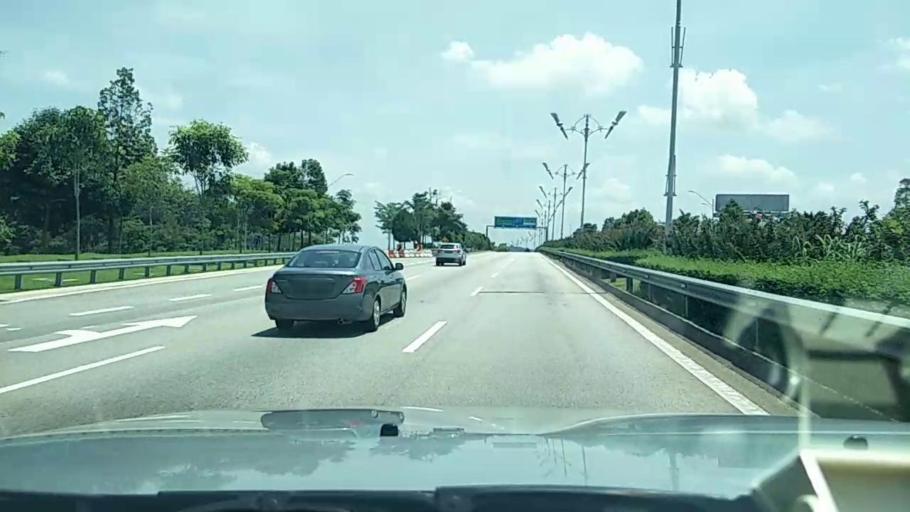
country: MY
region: Putrajaya
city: Putrajaya
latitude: 2.9572
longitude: 101.7082
